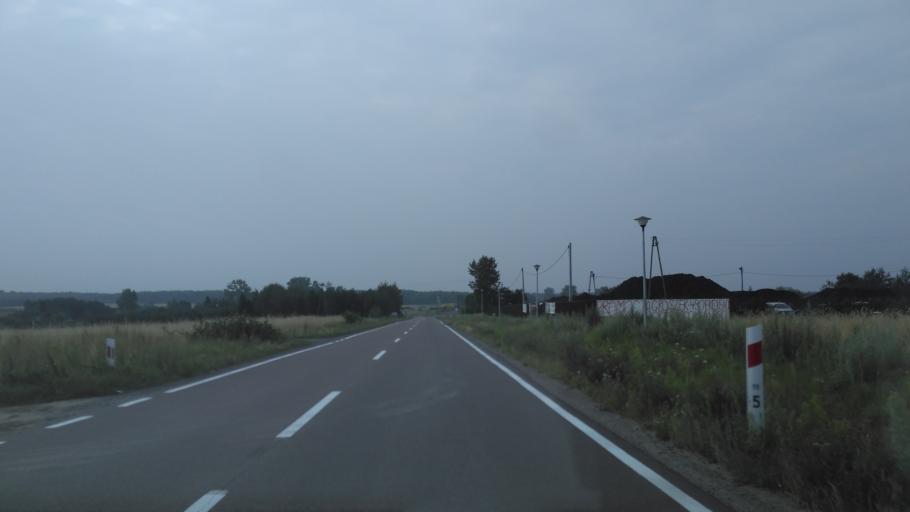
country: PL
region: Lublin Voivodeship
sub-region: Powiat chelmski
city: Rejowiec Fabryczny
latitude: 51.1791
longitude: 23.1762
